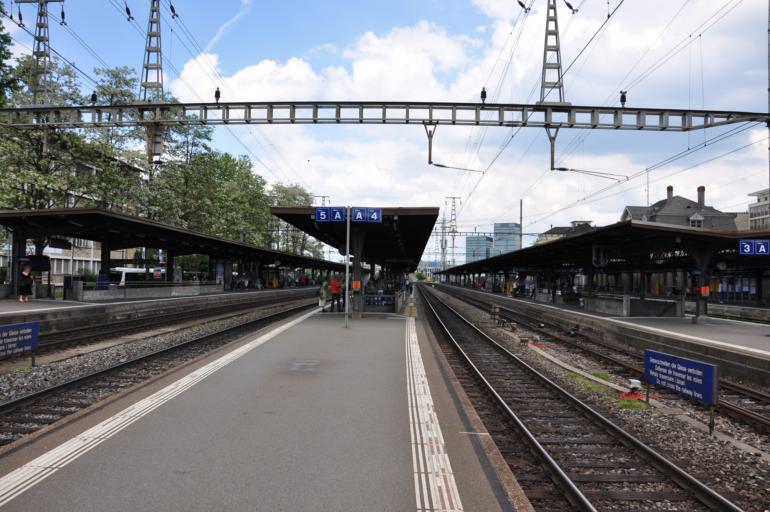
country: CH
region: Zurich
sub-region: Bezirk Zuerich
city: Zuerich (Kreis 11) / Oerlikon
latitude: 47.4109
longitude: 8.5420
